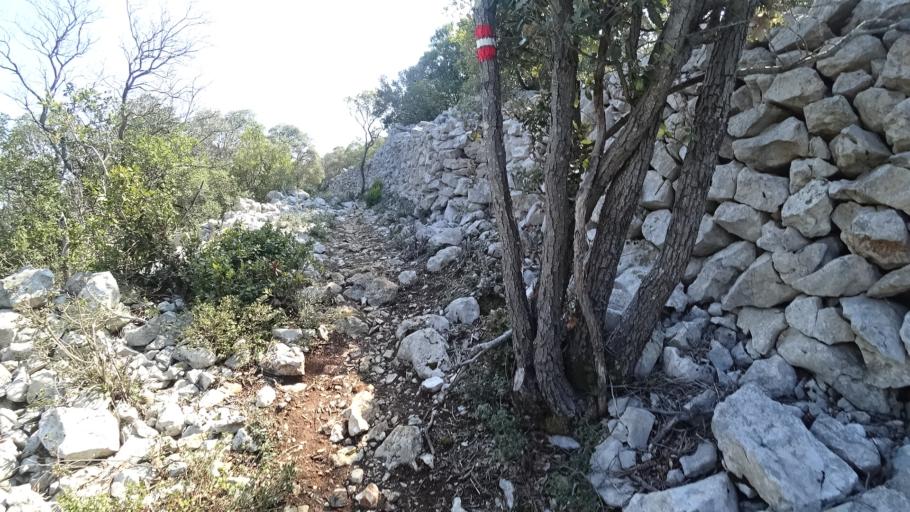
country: HR
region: Primorsko-Goranska
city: Mali Losinj
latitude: 44.4904
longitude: 14.5312
